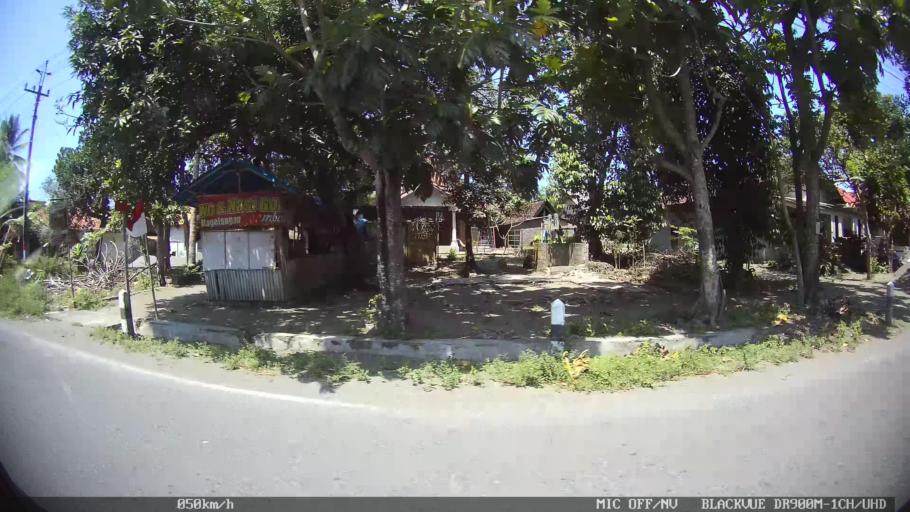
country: ID
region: Daerah Istimewa Yogyakarta
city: Srandakan
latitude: -7.9237
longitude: 110.1192
